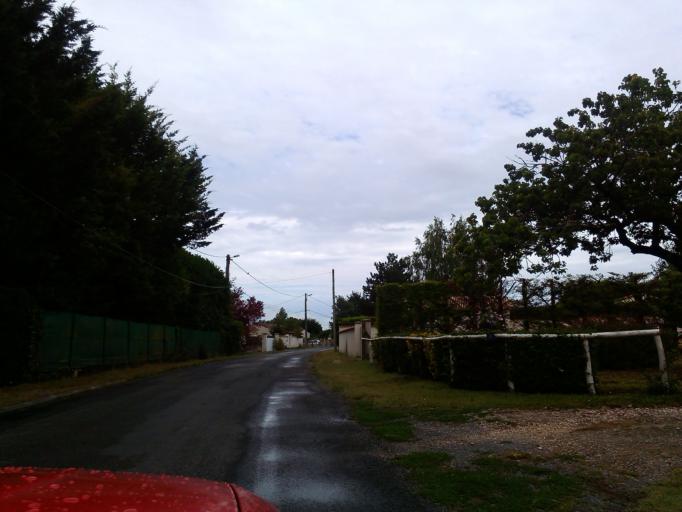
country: FR
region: Poitou-Charentes
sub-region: Departement de la Charente-Maritime
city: Arvert
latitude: 45.7386
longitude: -1.1301
